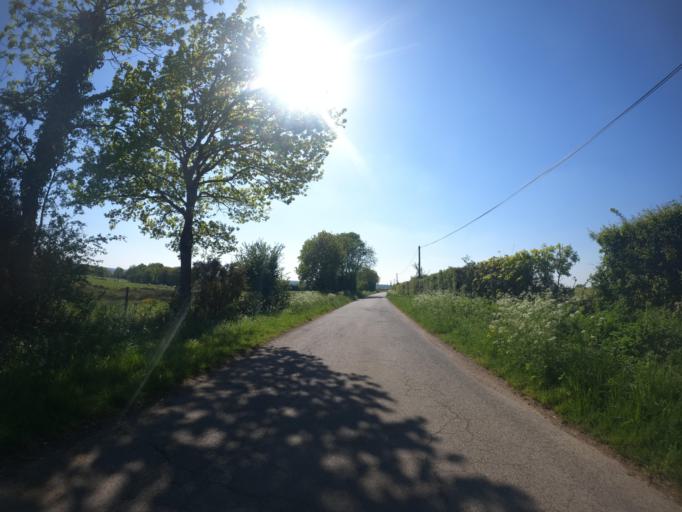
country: FR
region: Poitou-Charentes
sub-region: Departement des Deux-Sevres
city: Moncoutant
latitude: 46.6840
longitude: -0.5331
